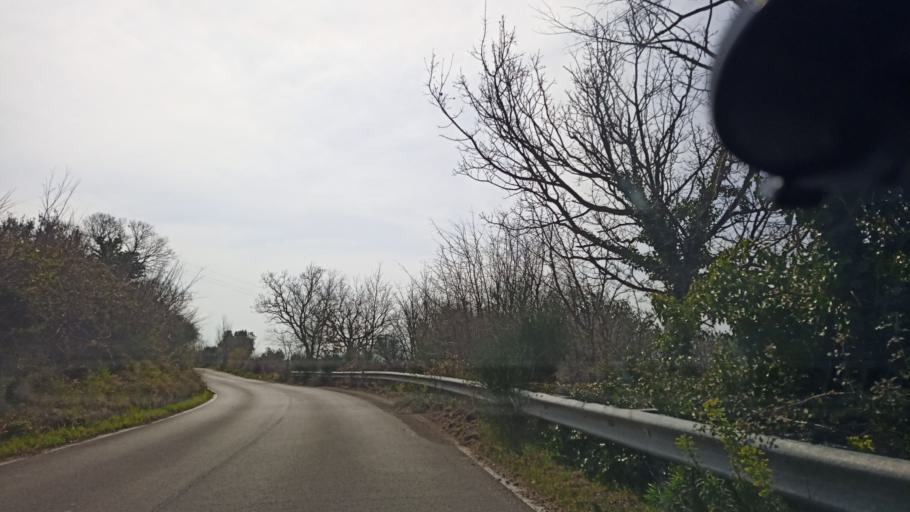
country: IT
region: Latium
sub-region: Provincia di Rieti
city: Montasola
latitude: 42.3690
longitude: 12.6763
